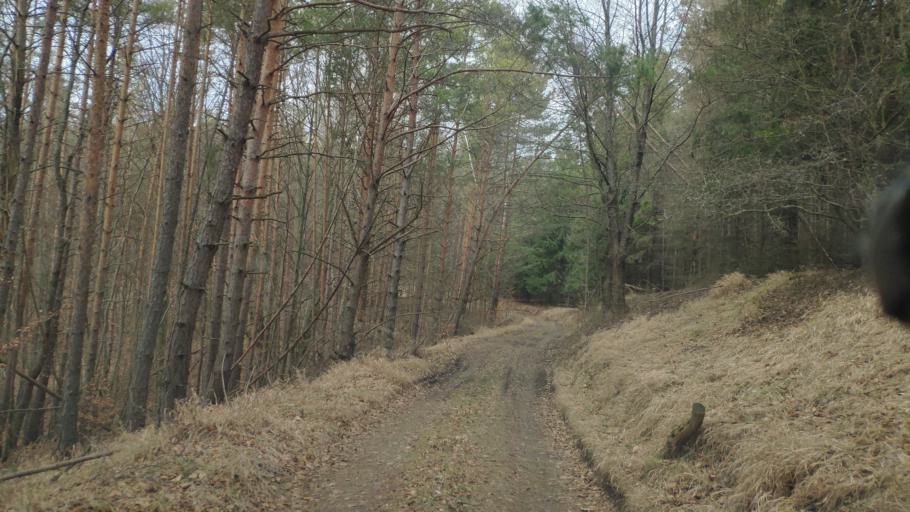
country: SK
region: Presovsky
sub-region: Okres Presov
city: Presov
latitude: 48.8974
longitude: 21.1688
